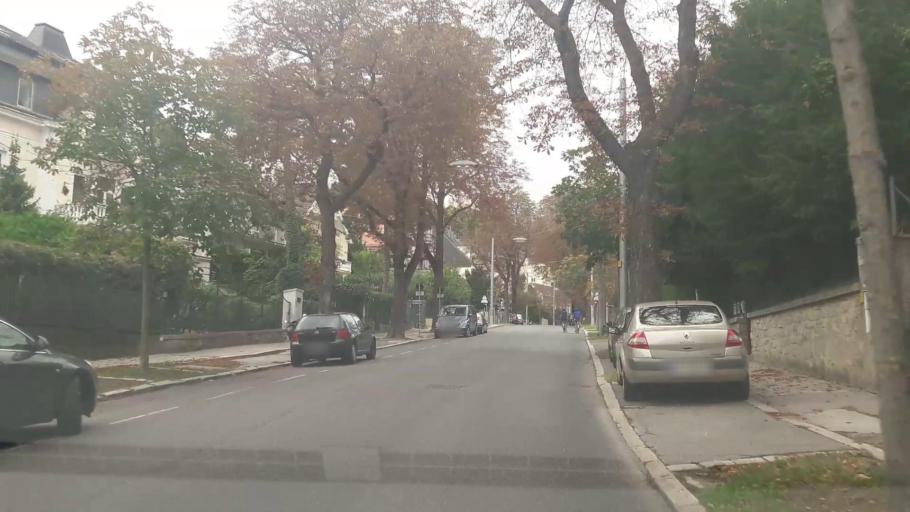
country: AT
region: Lower Austria
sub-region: Politischer Bezirk Korneuburg
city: Langenzersdorf
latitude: 48.2604
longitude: 16.3338
